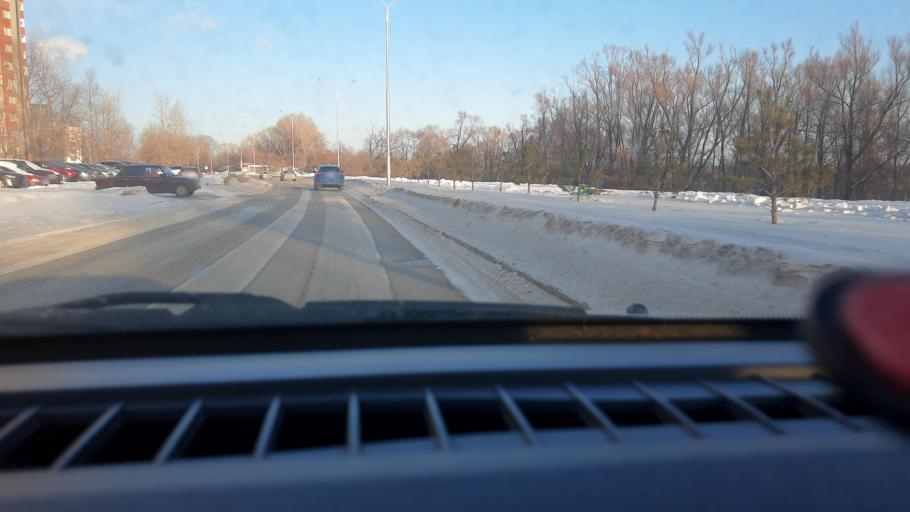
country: RU
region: Bashkortostan
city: Ufa
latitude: 54.7590
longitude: 56.0662
